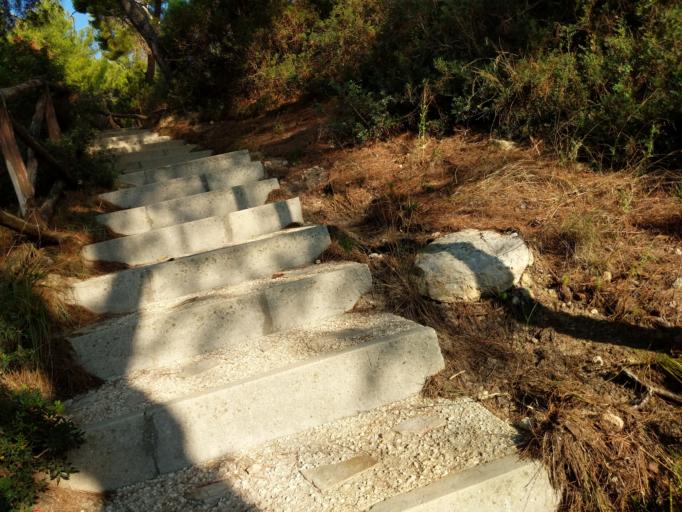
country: IT
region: Apulia
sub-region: Provincia di Foggia
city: Isole Tremiti
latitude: 42.1148
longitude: 15.4930
